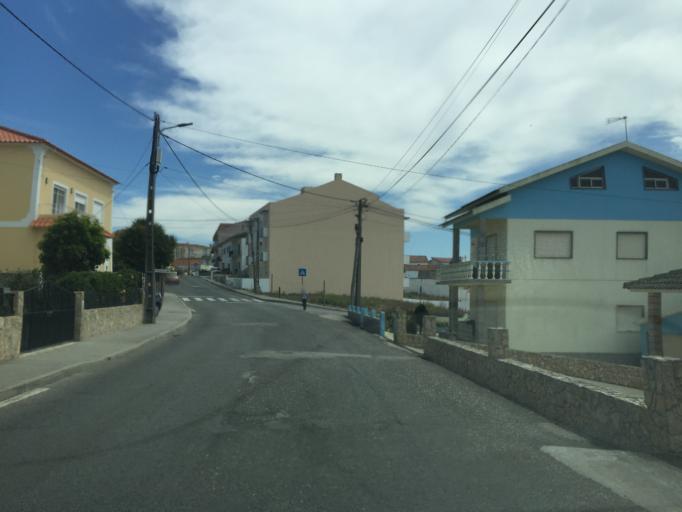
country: PT
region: Lisbon
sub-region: Lourinha
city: Lourinha
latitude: 39.2020
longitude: -9.3338
